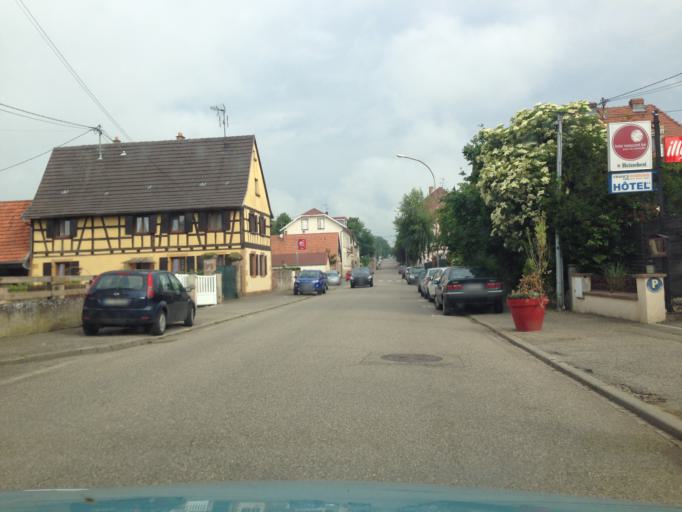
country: FR
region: Alsace
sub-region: Departement du Bas-Rhin
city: Bouxwiller
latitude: 48.8267
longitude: 7.4787
